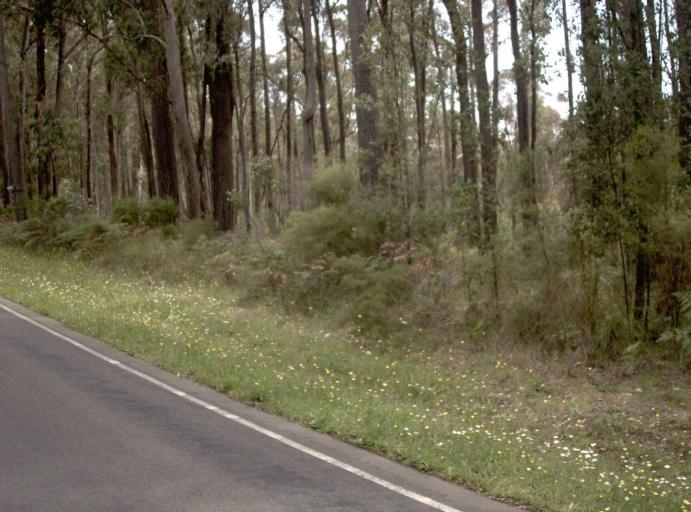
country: AU
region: Victoria
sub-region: Latrobe
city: Morwell
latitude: -38.0433
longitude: 146.4214
